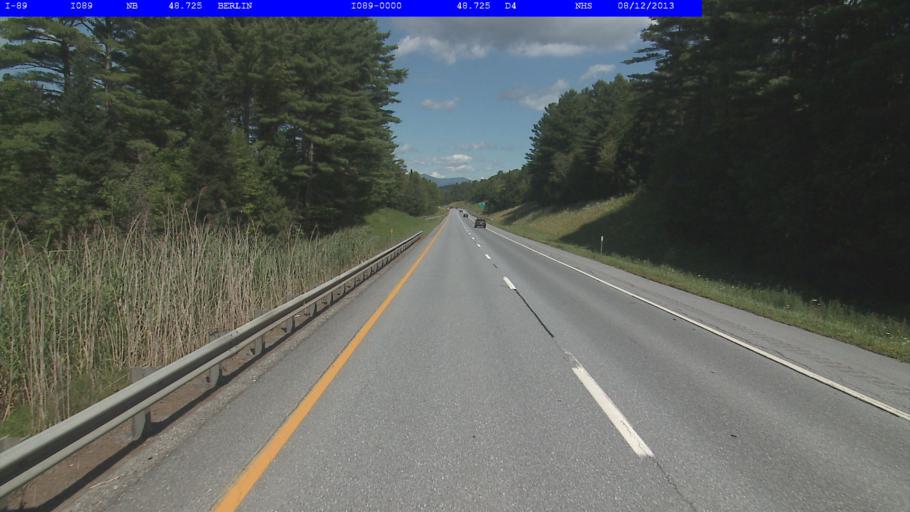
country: US
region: Vermont
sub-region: Washington County
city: Montpelier
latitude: 44.1937
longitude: -72.5766
